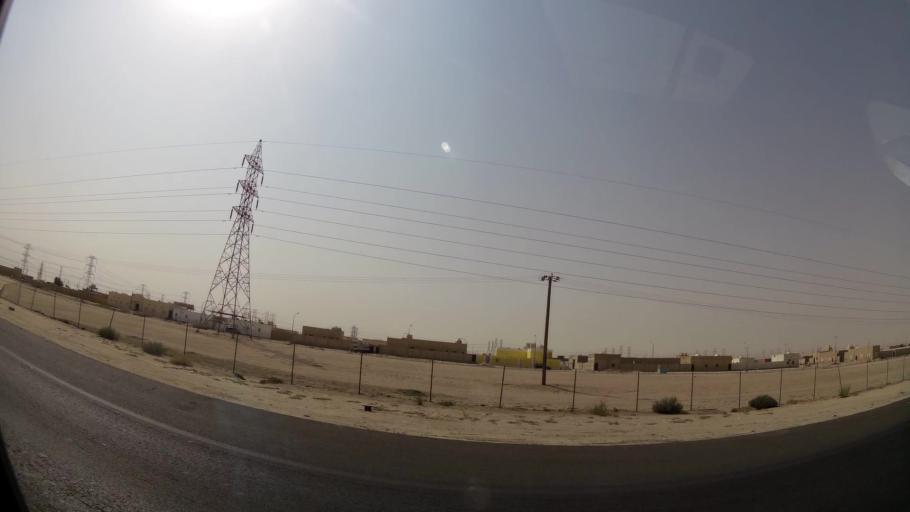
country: KW
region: Muhafazat al Jahra'
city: Al Jahra'
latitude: 29.3074
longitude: 47.6646
